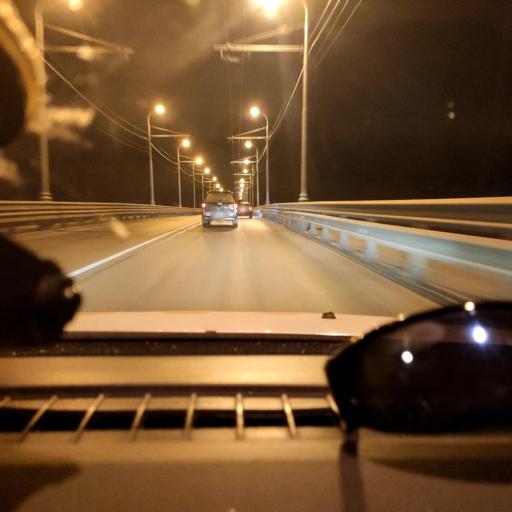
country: RU
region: Samara
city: Rozhdestveno
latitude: 53.1735
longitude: 50.0739
